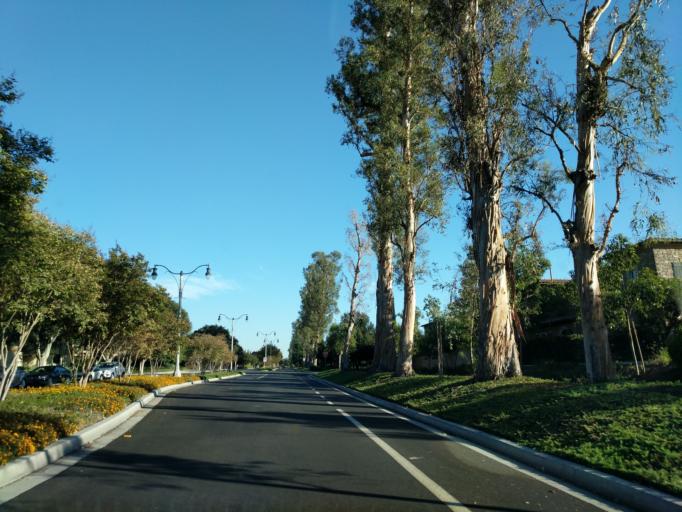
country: US
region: California
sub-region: Orange County
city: Irvine
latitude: 33.6951
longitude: -117.7534
